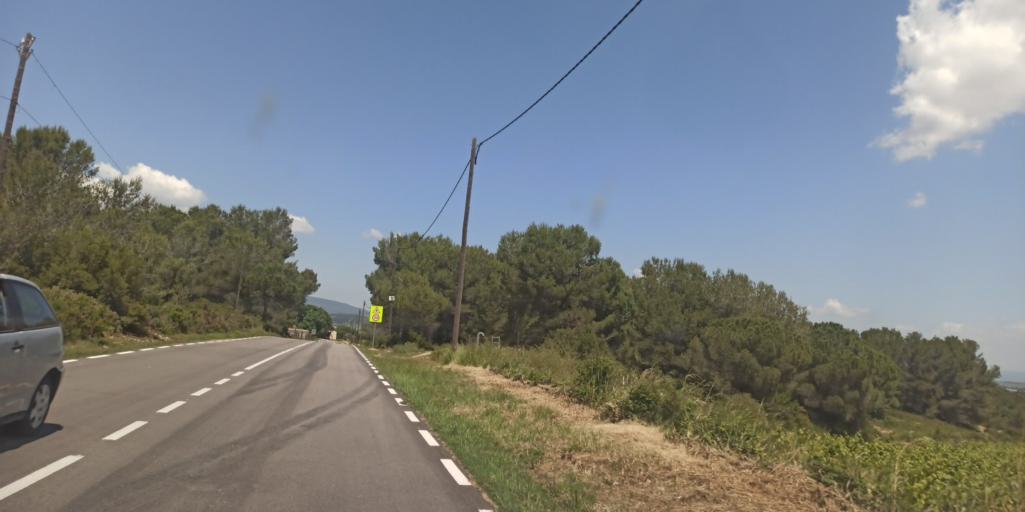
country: ES
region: Catalonia
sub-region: Provincia de Barcelona
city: Vilafranca del Penedes
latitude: 41.3094
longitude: 1.6922
